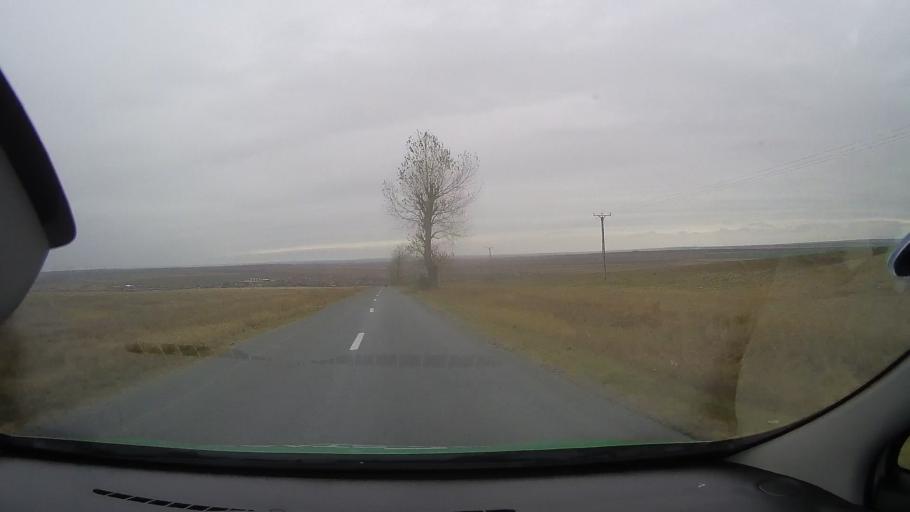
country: RO
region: Constanta
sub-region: Comuna Pantelimon
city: Pantelimon
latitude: 44.5896
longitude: 28.3181
